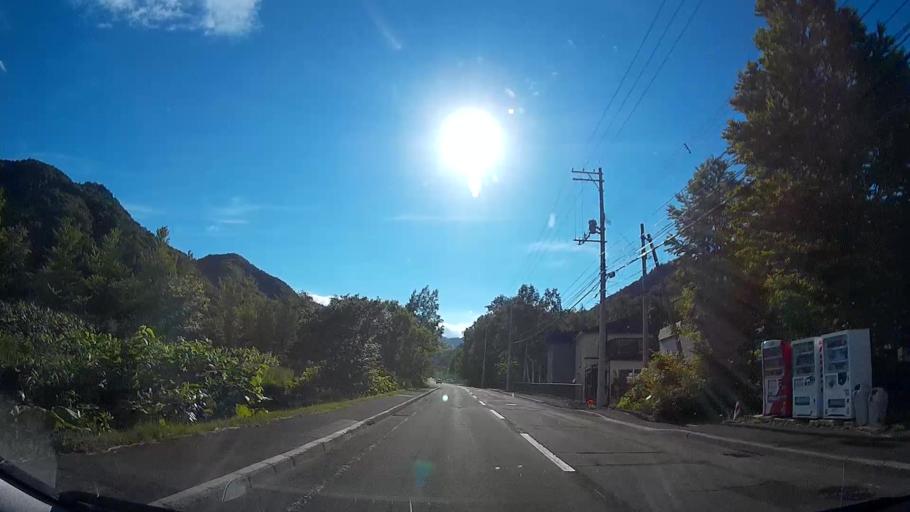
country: JP
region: Hokkaido
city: Sapporo
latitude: 42.9727
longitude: 141.1632
